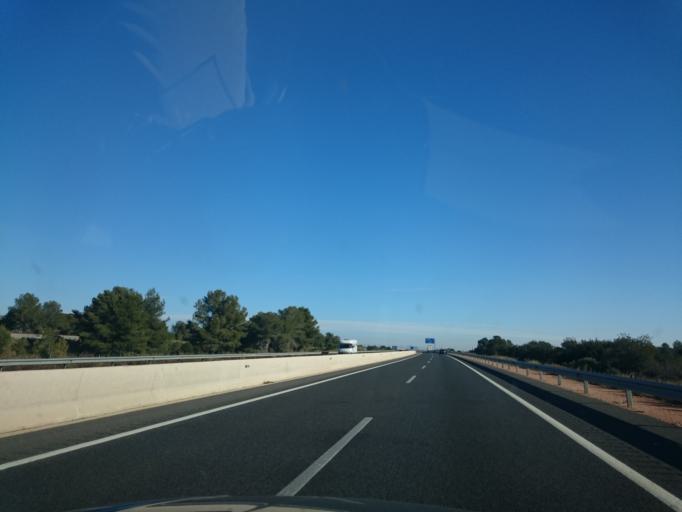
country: ES
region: Catalonia
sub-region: Provincia de Tarragona
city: Cambrils
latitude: 41.0504
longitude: 0.9784
